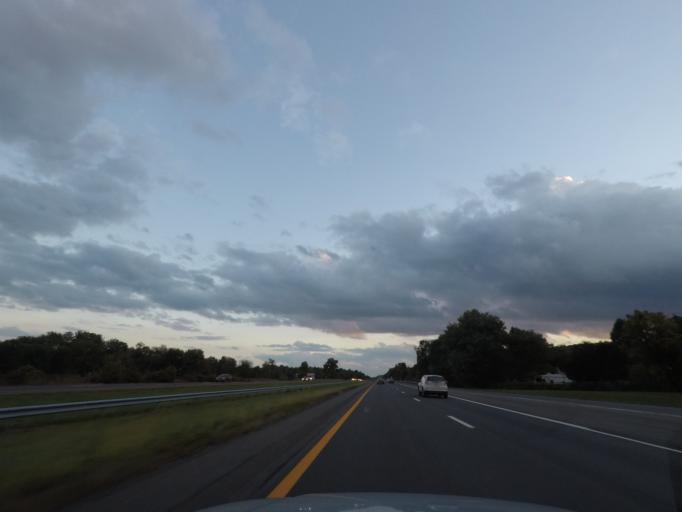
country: US
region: New York
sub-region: Ulster County
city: Lake Katrine
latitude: 42.0126
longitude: -73.9995
